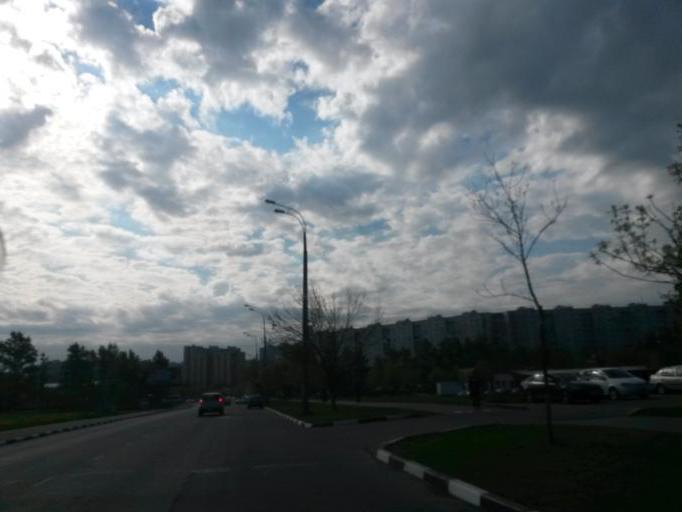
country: RU
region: Moscow
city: Mar'ino
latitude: 55.6541
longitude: 37.7188
